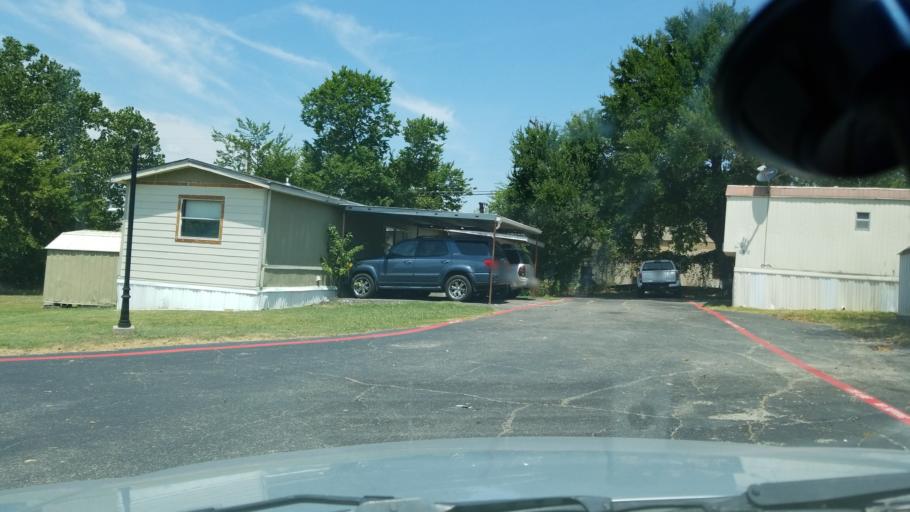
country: US
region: Texas
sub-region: Dallas County
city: Irving
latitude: 32.8192
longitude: -96.9960
